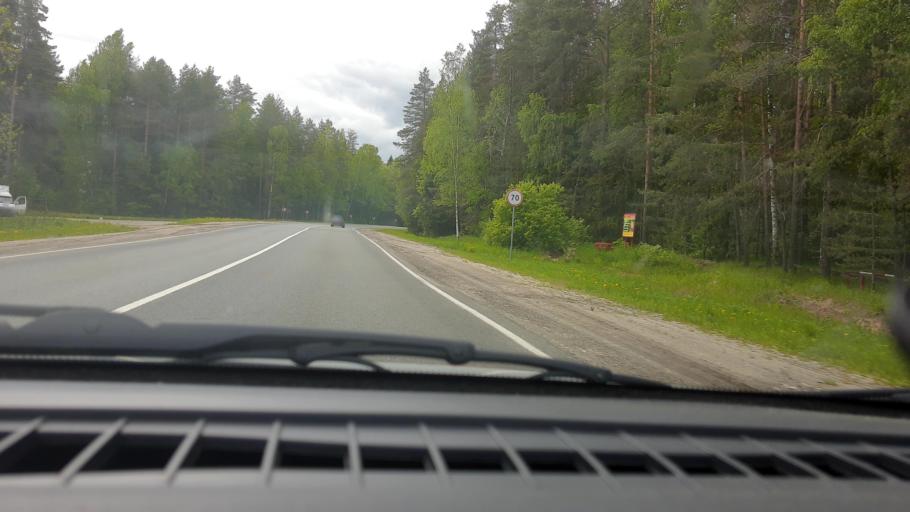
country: RU
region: Nizjnij Novgorod
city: Semenov
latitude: 56.7471
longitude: 44.3566
